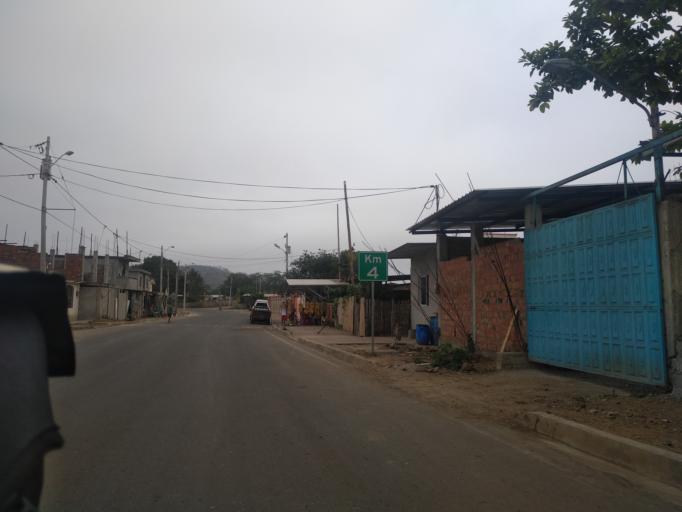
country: EC
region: Manabi
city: Montecristi
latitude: -1.0835
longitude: -80.6807
